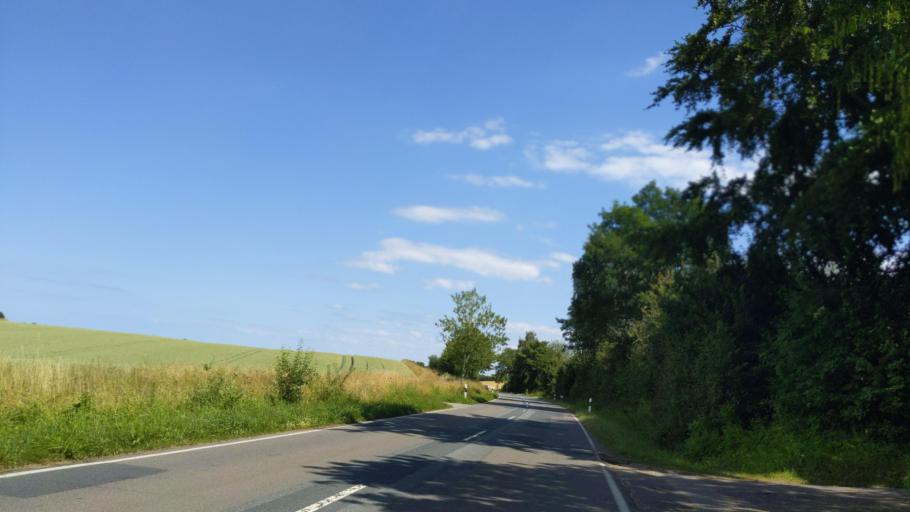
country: DE
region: Schleswig-Holstein
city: Manhagen
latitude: 54.1570
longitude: 10.9228
